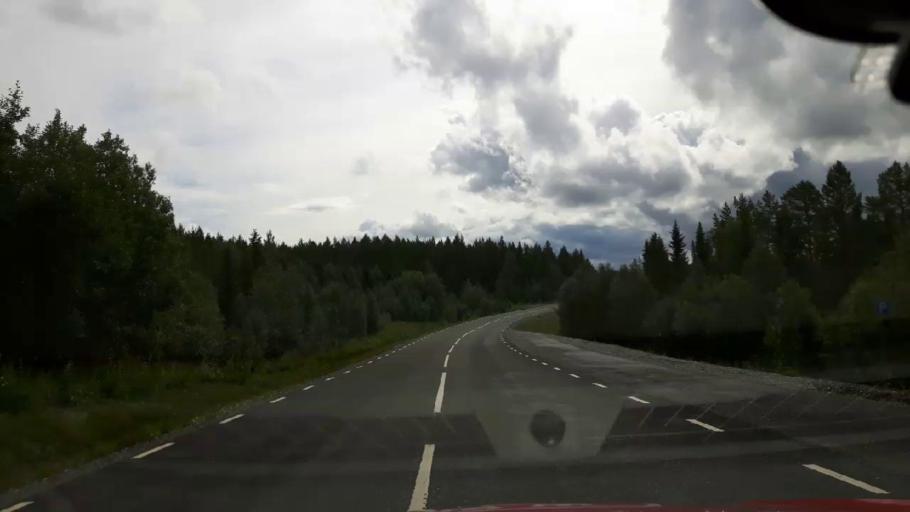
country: NO
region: Nord-Trondelag
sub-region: Lierne
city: Sandvika
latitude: 64.6087
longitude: 14.1195
